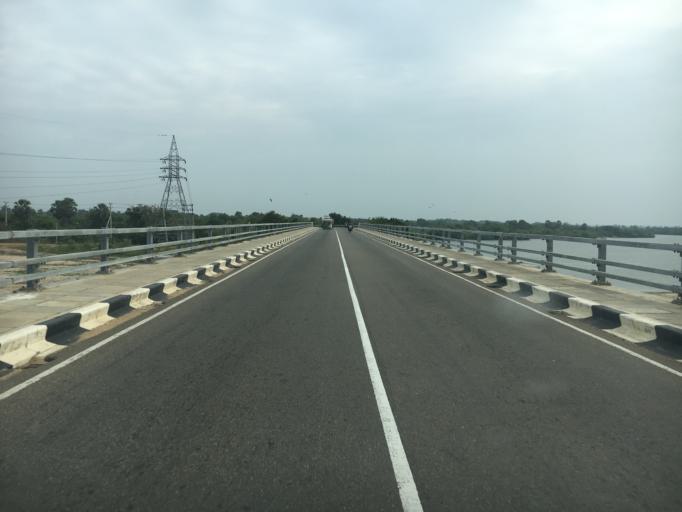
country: LK
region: Eastern Province
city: Trincomalee
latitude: 8.4700
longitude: 81.2026
